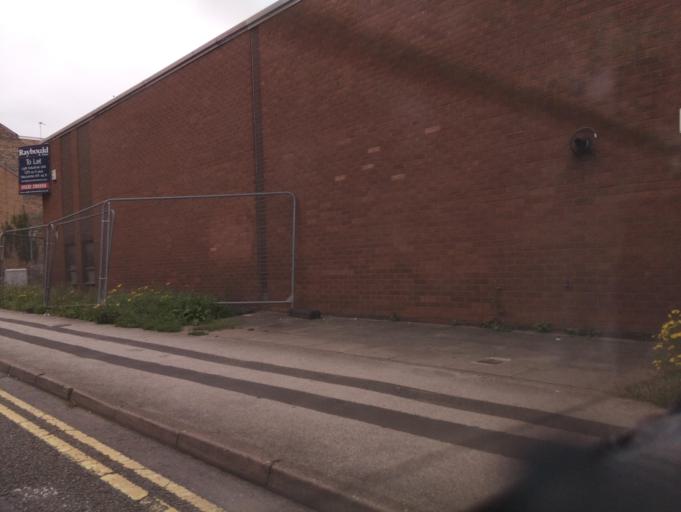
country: GB
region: England
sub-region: Derby
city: Derby
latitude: 52.9153
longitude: -1.4834
